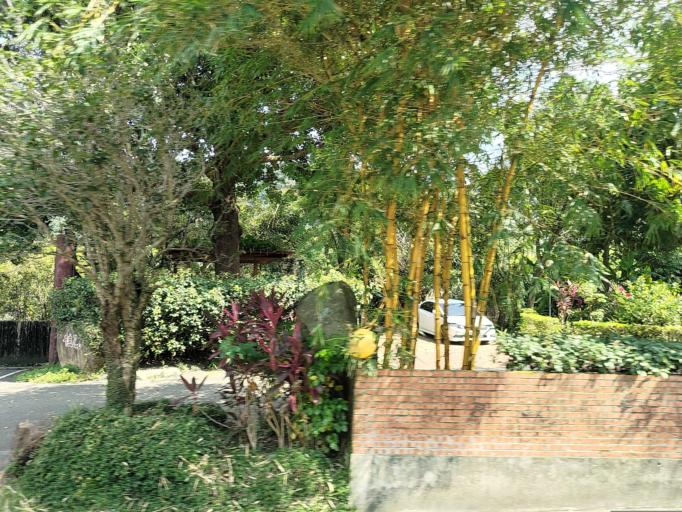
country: TW
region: Taiwan
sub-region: Miaoli
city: Miaoli
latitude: 24.5953
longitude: 121.0019
